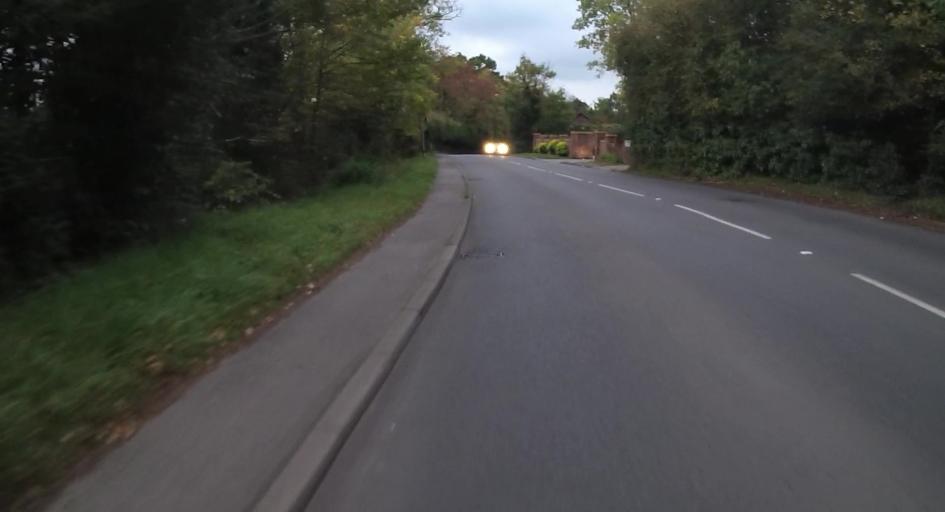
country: GB
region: England
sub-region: Wokingham
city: Finchampstead
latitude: 51.3648
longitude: -0.8553
